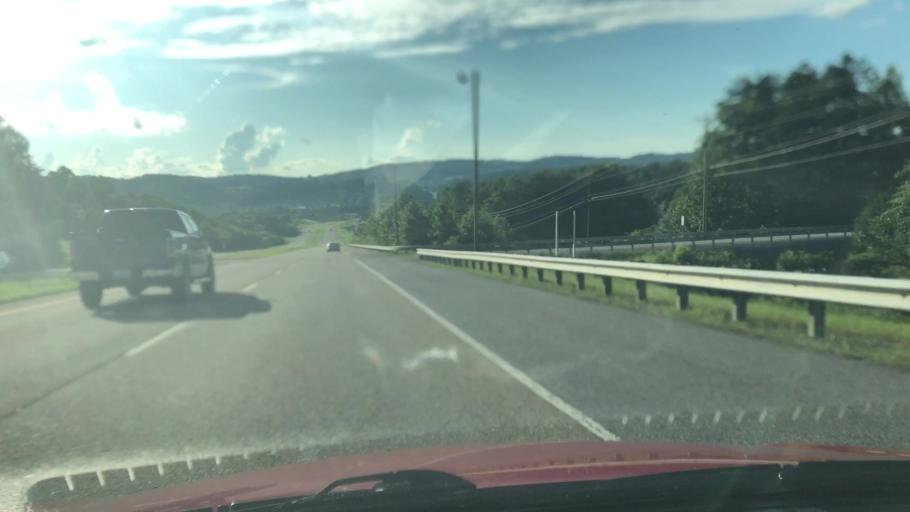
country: US
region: Tennessee
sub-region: Jefferson County
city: Dandridge
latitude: 36.0415
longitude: -83.4475
